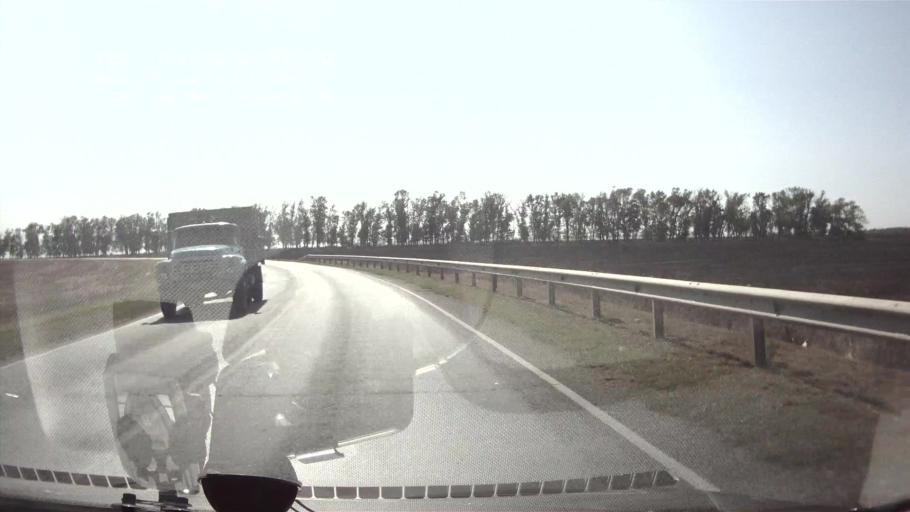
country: RU
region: Krasnodarskiy
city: Dmitriyevskaya
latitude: 45.7044
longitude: 40.7251
